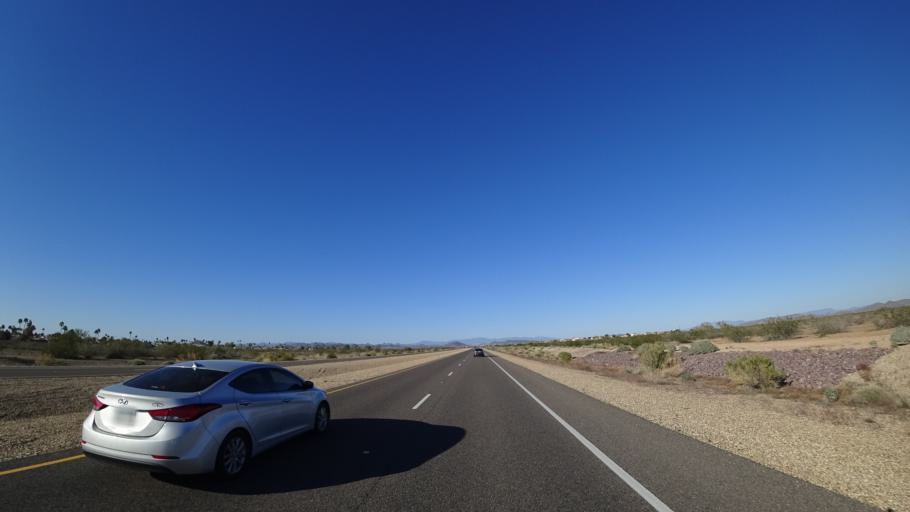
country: US
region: Arizona
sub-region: Maricopa County
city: Sun City West
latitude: 33.6719
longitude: -112.3228
